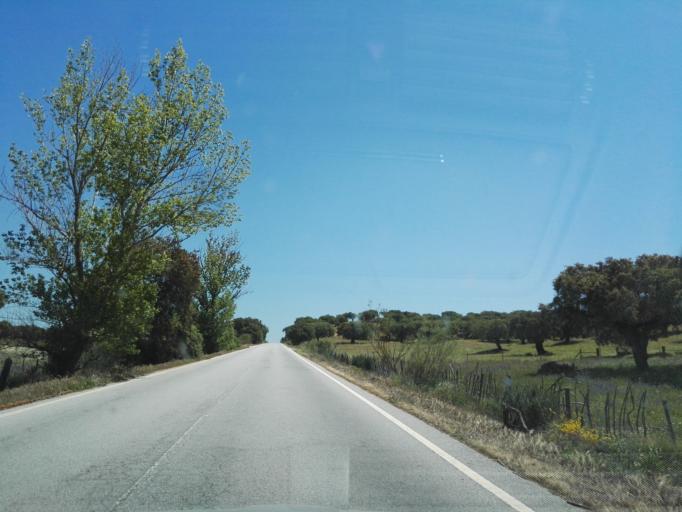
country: PT
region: Portalegre
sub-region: Elvas
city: Elvas
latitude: 38.9975
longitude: -7.1810
